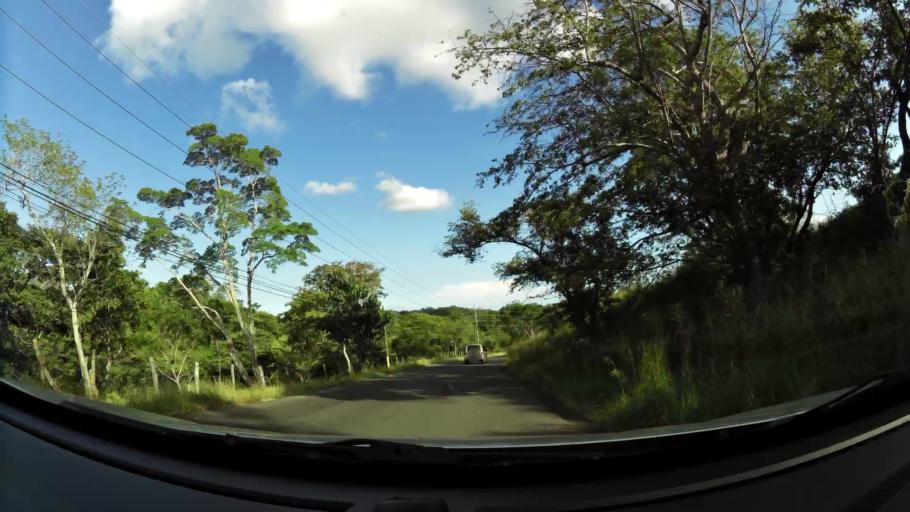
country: CR
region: Guanacaste
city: Sardinal
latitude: 10.5407
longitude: -85.6712
